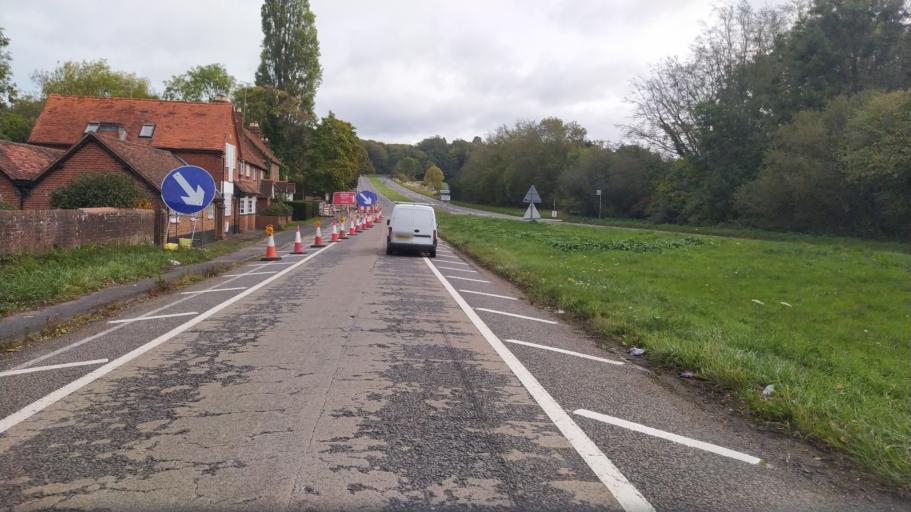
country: GB
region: England
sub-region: Hampshire
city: Eversley
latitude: 51.3144
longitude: -0.8895
